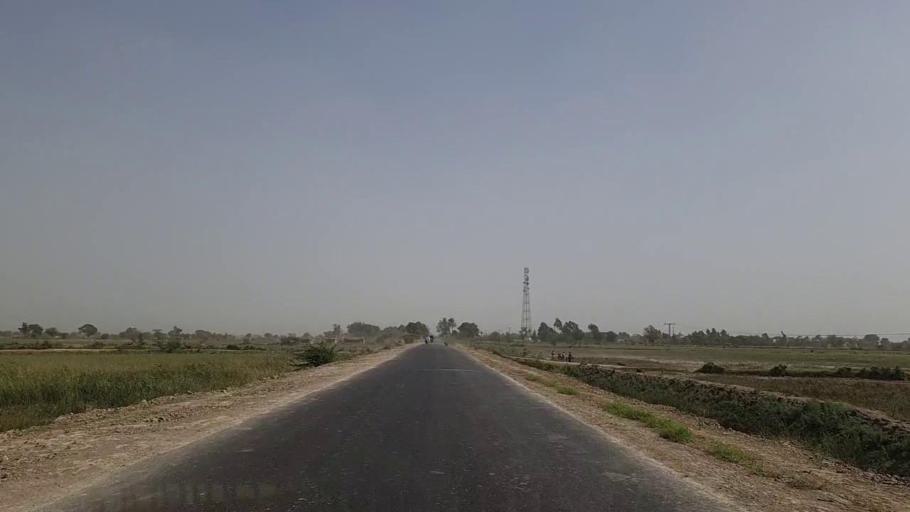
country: PK
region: Sindh
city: Tando Bago
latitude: 24.8184
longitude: 68.9054
